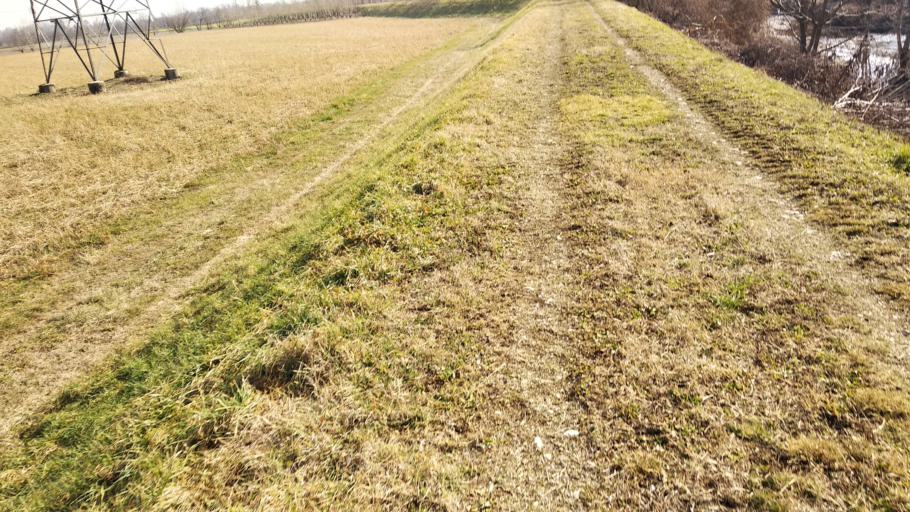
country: IT
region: Veneto
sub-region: Provincia di Vicenza
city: Motta
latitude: 45.5922
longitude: 11.5009
